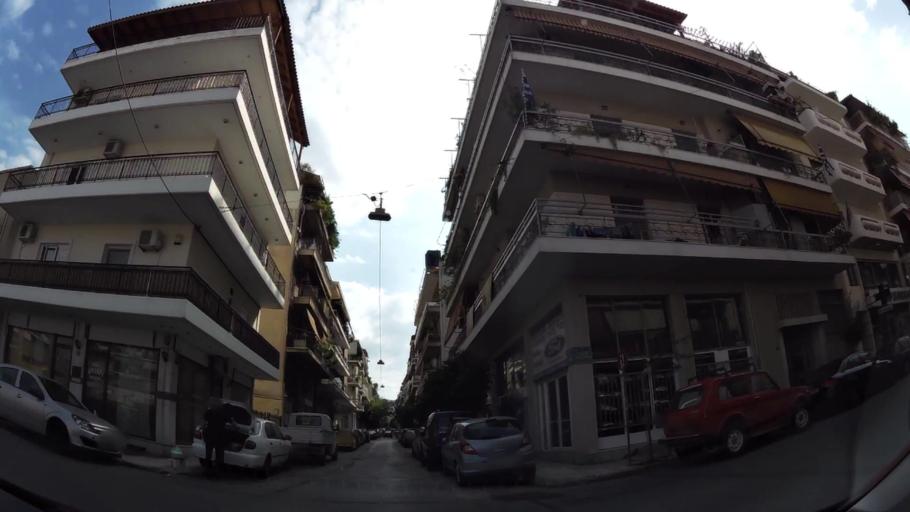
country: GR
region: Attica
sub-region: Nomarchia Athinas
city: Dhafni
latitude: 37.9604
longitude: 23.7264
